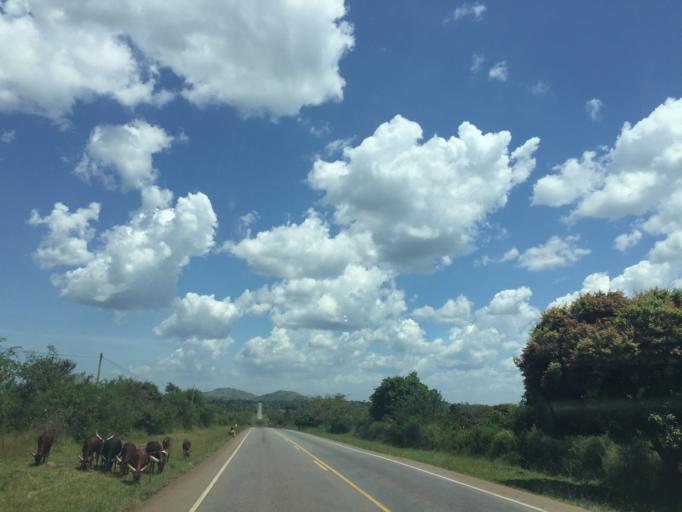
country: UG
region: Central Region
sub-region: Nakasongola District
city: Nakasongola
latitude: 1.3405
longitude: 32.3983
